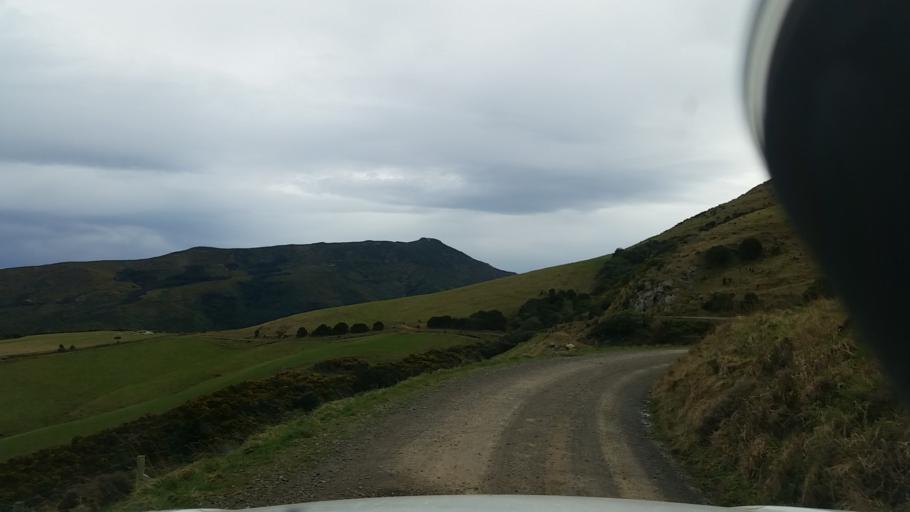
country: NZ
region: Canterbury
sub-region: Christchurch City
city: Christchurch
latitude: -43.8186
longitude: 173.0620
